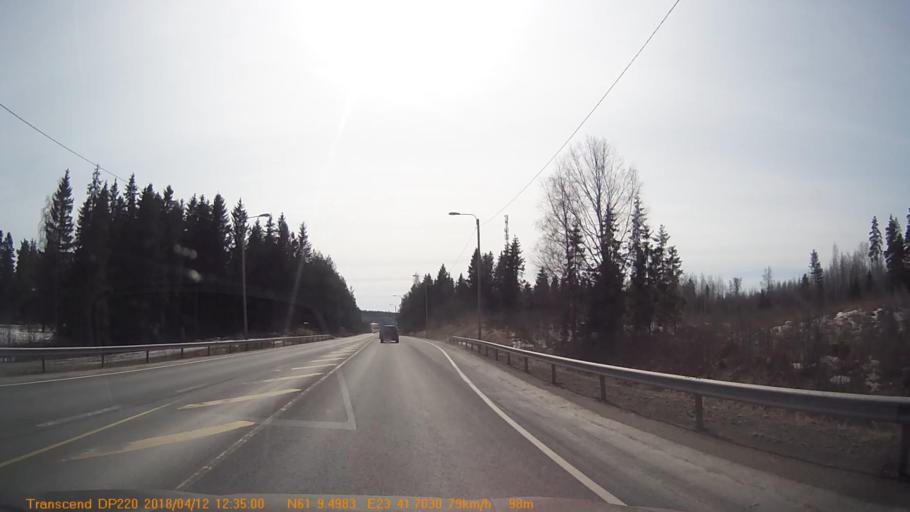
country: FI
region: Pirkanmaa
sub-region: Etelae-Pirkanmaa
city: Kylmaekoski
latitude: 61.1584
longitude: 23.6951
